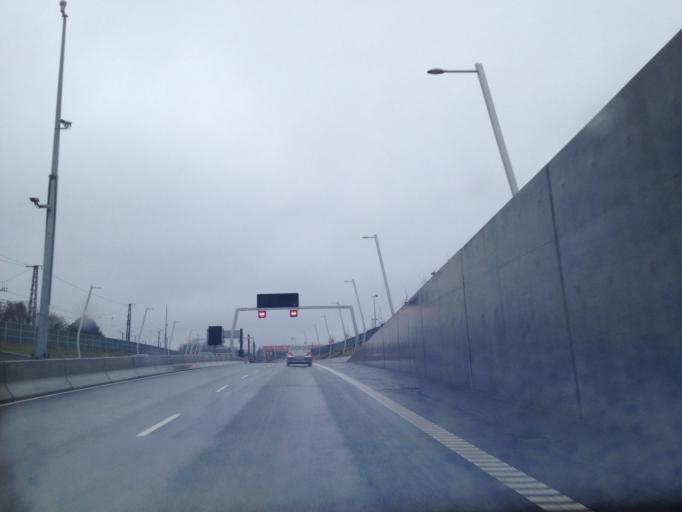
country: DK
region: Capital Region
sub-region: Kobenhavn
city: Copenhagen
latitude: 55.7176
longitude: 12.5686
